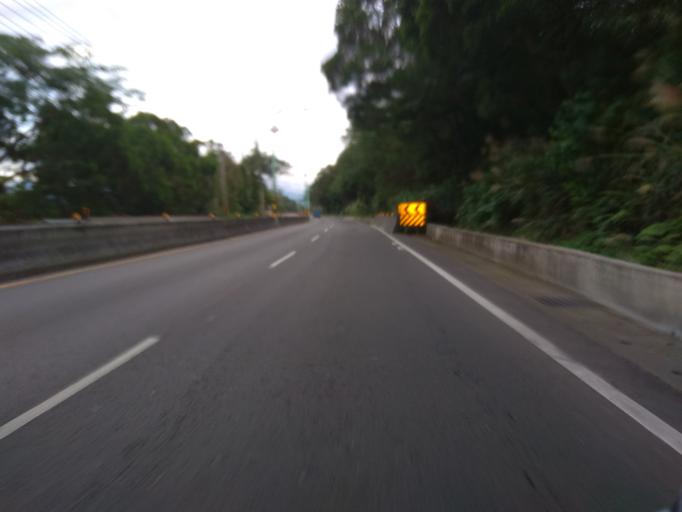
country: TW
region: Taiwan
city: Daxi
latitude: 24.8483
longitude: 121.2073
